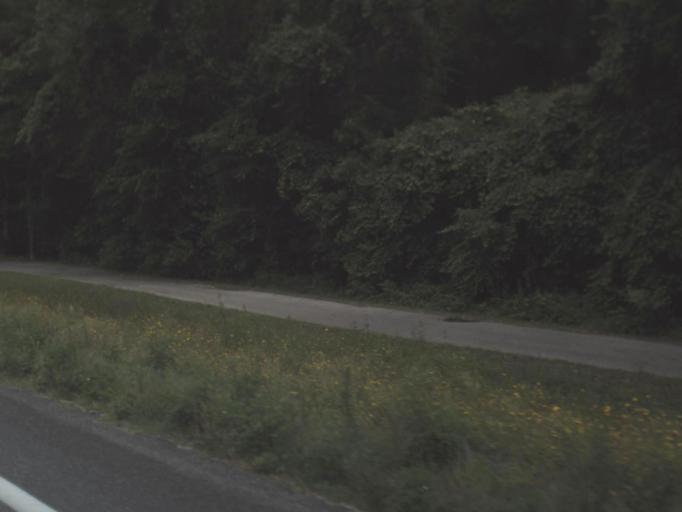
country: US
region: Florida
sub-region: Suwannee County
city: Wellborn
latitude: 29.9525
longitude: -82.8920
